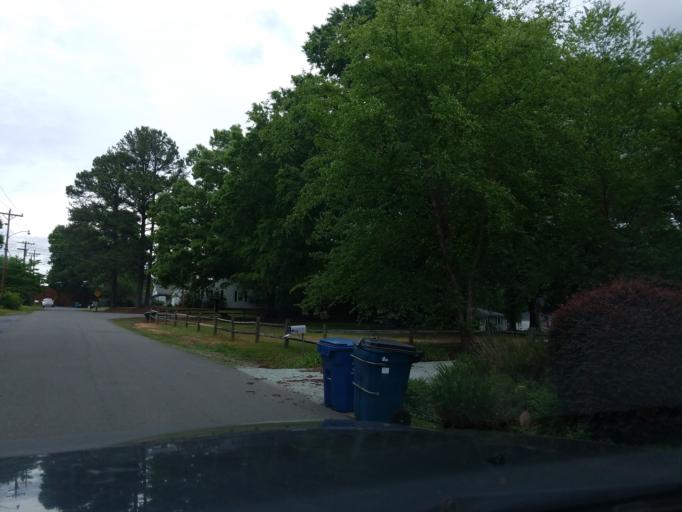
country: US
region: North Carolina
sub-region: Durham County
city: Durham
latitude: 36.0269
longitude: -78.9282
